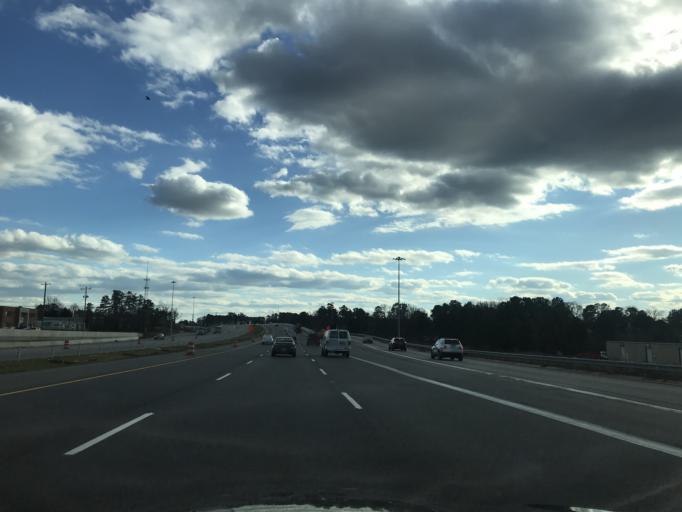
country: US
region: North Carolina
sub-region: Durham County
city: Durham
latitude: 35.9954
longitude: -78.8632
